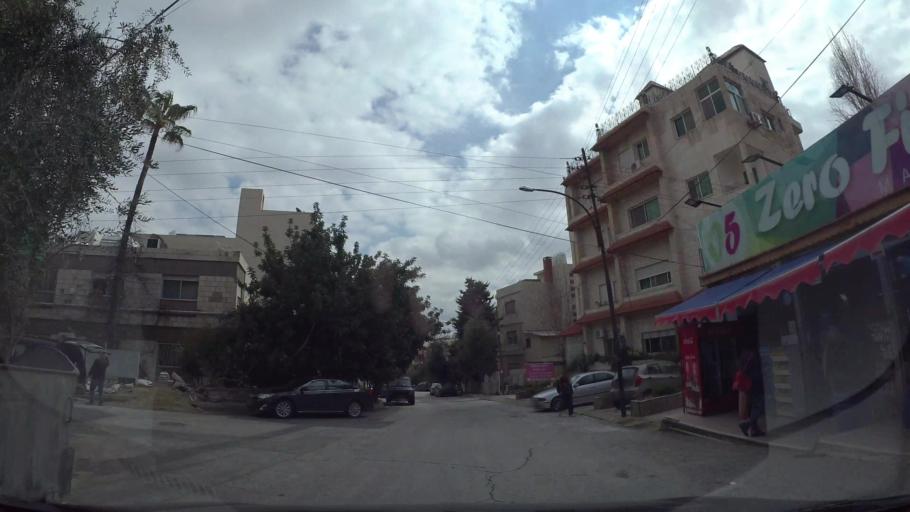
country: JO
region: Amman
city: Amman
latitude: 31.9735
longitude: 35.9029
